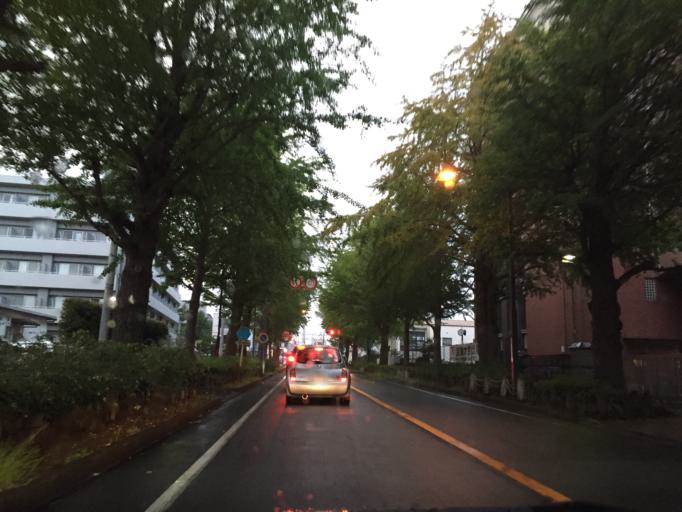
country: JP
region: Shizuoka
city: Mishima
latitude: 35.1336
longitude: 138.9132
